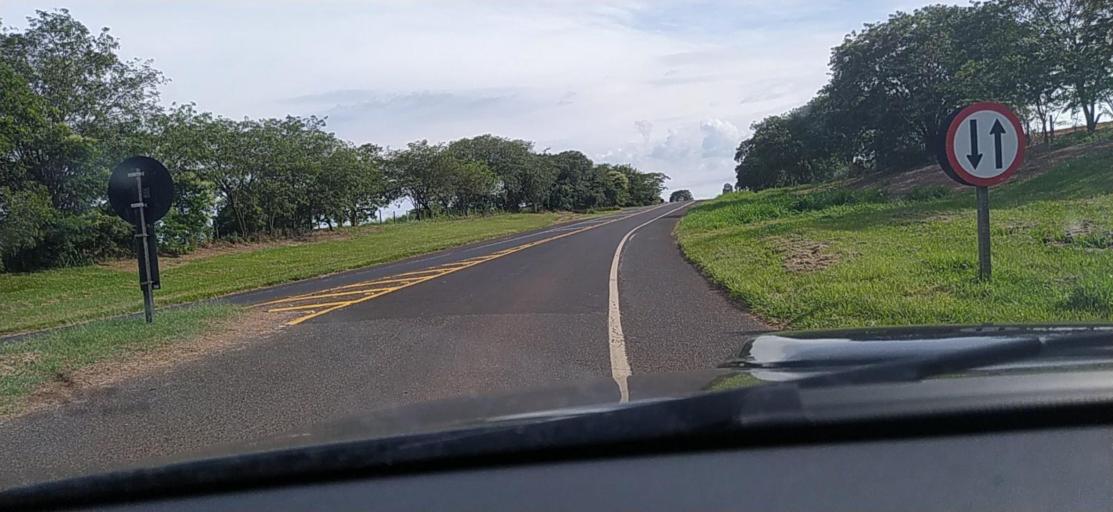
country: BR
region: Sao Paulo
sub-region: Catanduva
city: Catanduva
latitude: -21.0893
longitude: -49.0761
